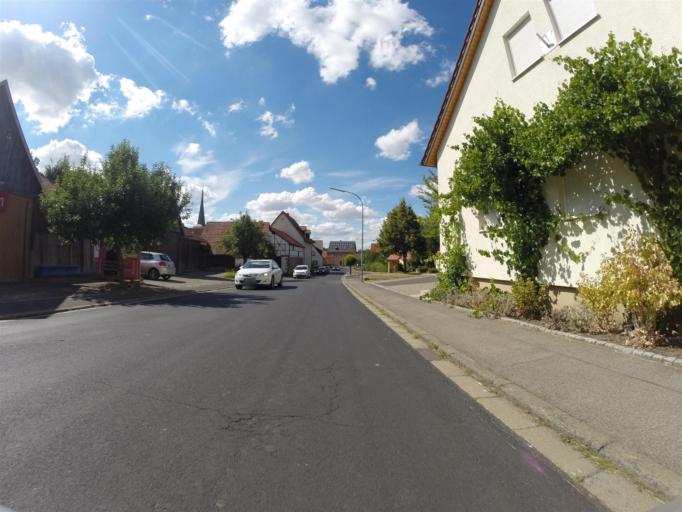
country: DE
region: Bavaria
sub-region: Regierungsbezirk Unterfranken
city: Donnersdorf
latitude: 49.9393
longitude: 10.4125
